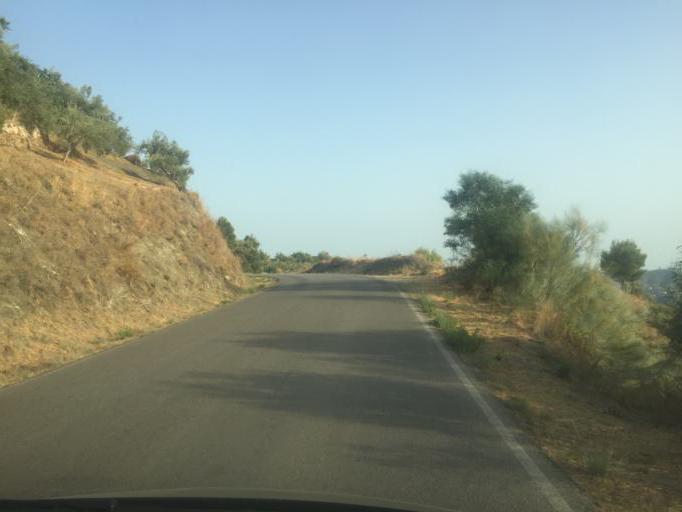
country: ES
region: Andalusia
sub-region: Provincia de Malaga
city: Frigiliana
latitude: 36.8028
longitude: -3.9126
